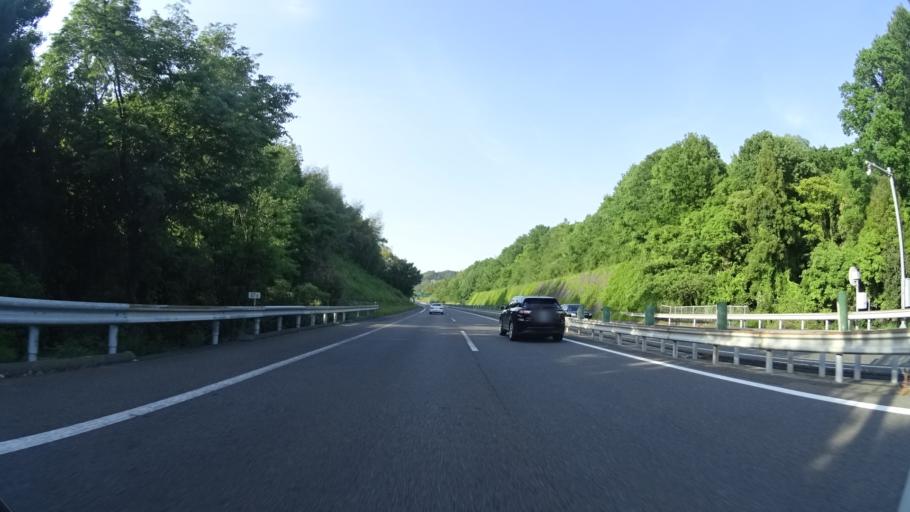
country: JP
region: Ehime
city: Kawanoecho
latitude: 33.9926
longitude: 133.5944
